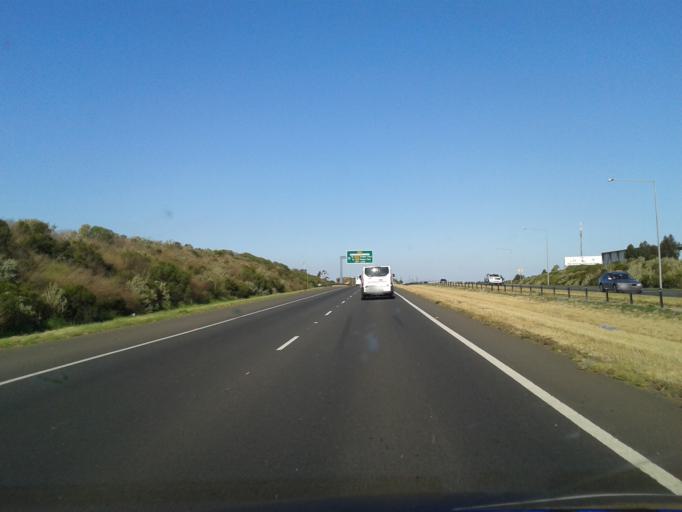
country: AU
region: Victoria
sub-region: Brimbank
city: Derrimut
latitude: -37.7984
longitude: 144.7727
